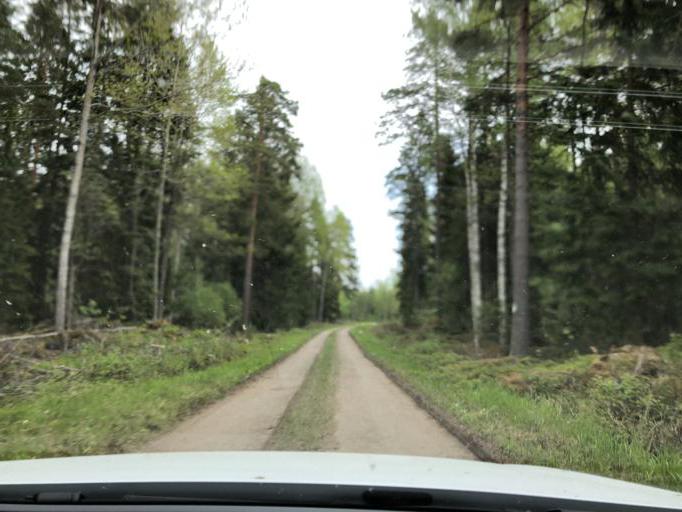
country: SE
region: Uppsala
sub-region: Heby Kommun
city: OEstervala
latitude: 60.3737
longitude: 17.2380
